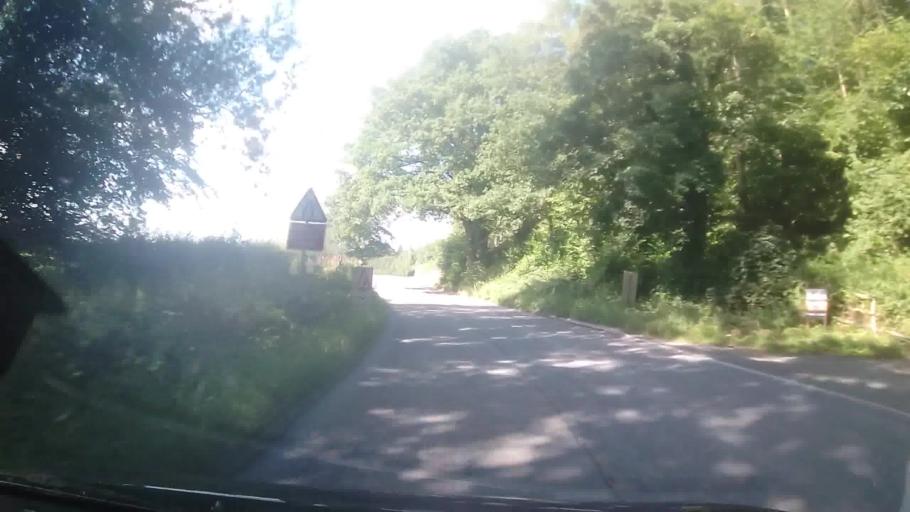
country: GB
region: England
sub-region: Shropshire
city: Bicton
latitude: 52.7606
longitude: -2.8109
